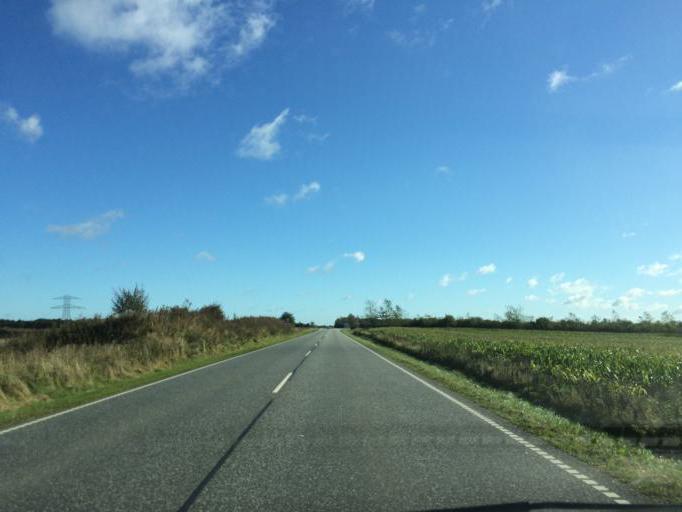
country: DK
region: Central Jutland
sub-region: Holstebro Kommune
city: Vinderup
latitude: 56.3985
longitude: 8.8988
